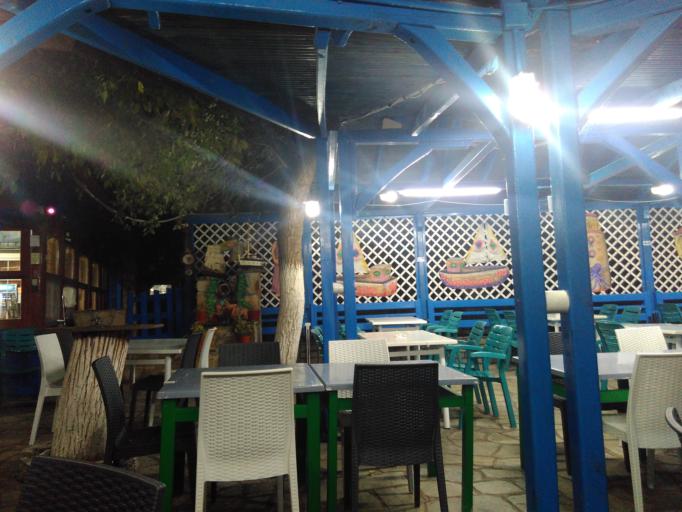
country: GR
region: East Macedonia and Thrace
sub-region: Nomos Rodopis
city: Xylagani
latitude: 40.8744
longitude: 25.5096
